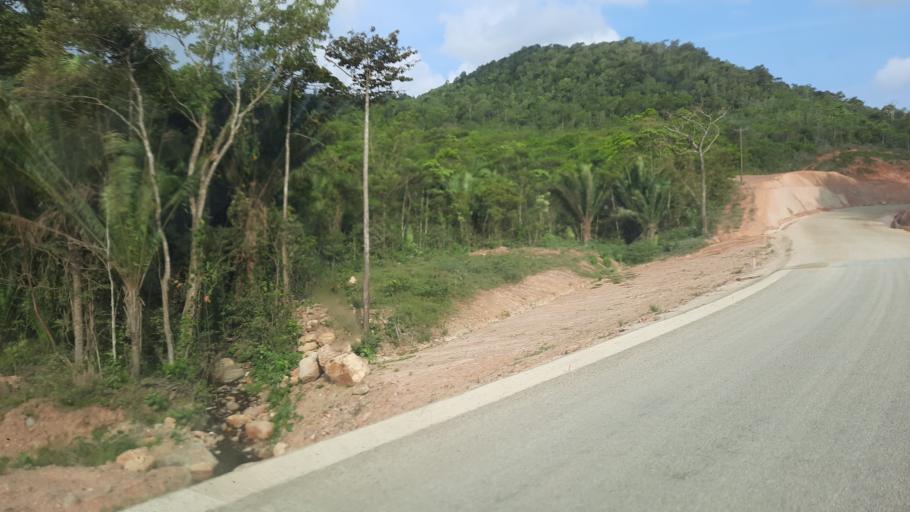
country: BZ
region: Cayo
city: Belmopan
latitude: 17.0594
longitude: -88.5871
